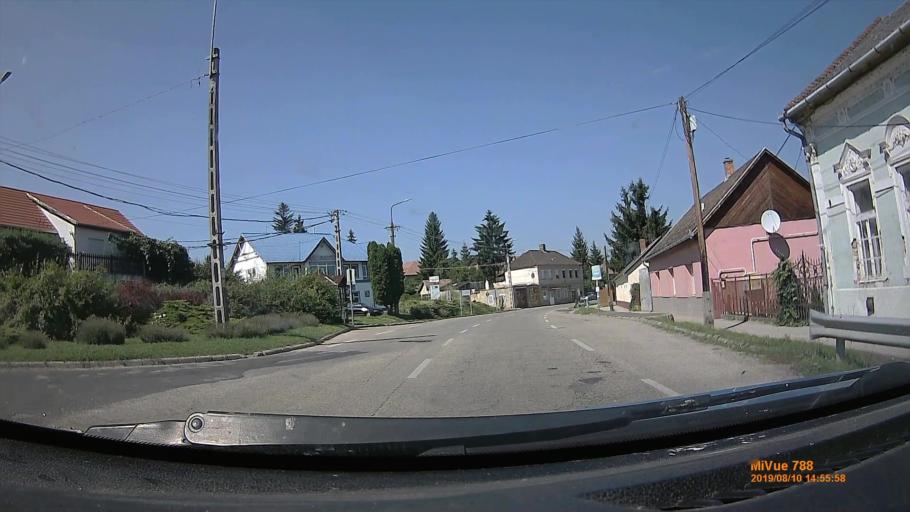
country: HU
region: Somogy
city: Lengyeltoti
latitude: 46.6643
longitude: 17.6352
